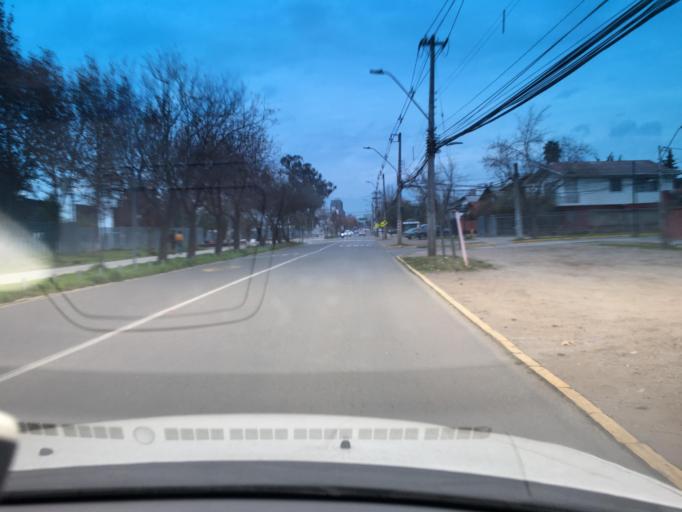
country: CL
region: Santiago Metropolitan
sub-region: Provincia de Santiago
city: Villa Presidente Frei, Nunoa, Santiago, Chile
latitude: -33.4659
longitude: -70.6067
